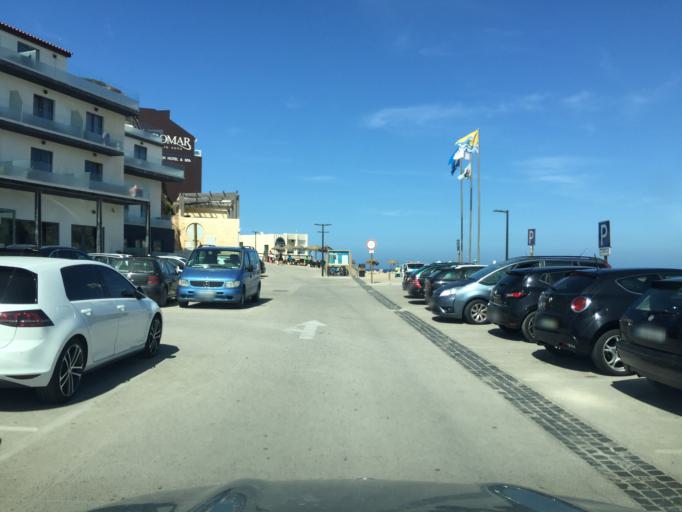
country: PT
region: Lisbon
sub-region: Torres Vedras
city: A dos Cunhados
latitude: 39.1775
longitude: -9.3548
